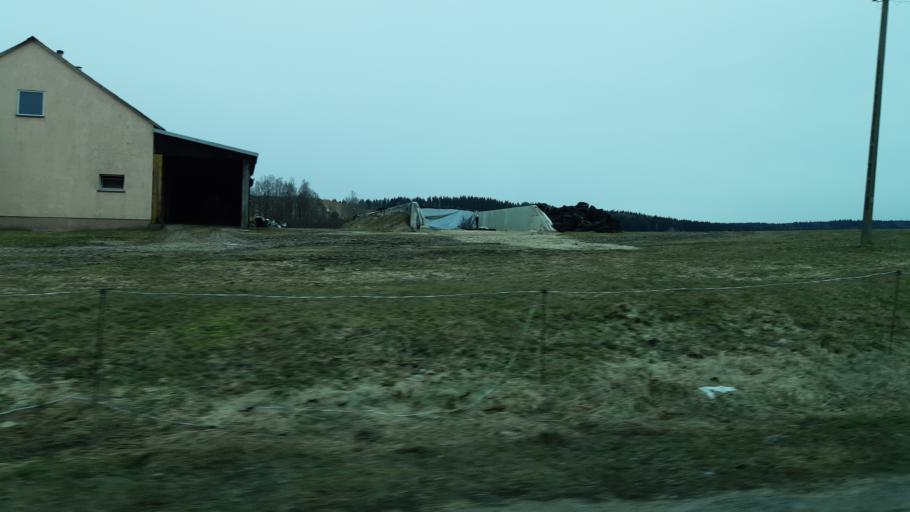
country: PL
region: Podlasie
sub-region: Suwalki
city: Suwalki
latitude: 54.3336
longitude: 22.9351
